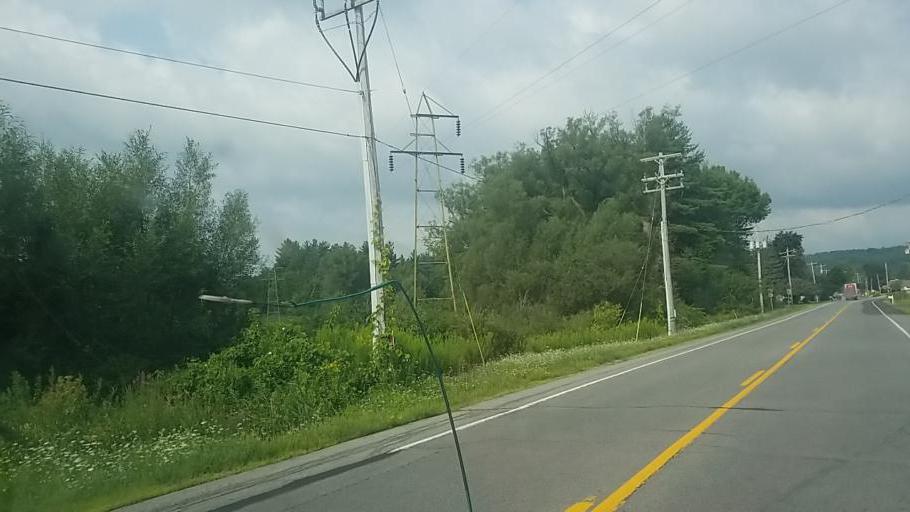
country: US
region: New York
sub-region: Fulton County
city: Gloversville
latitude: 43.0544
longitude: -74.3766
